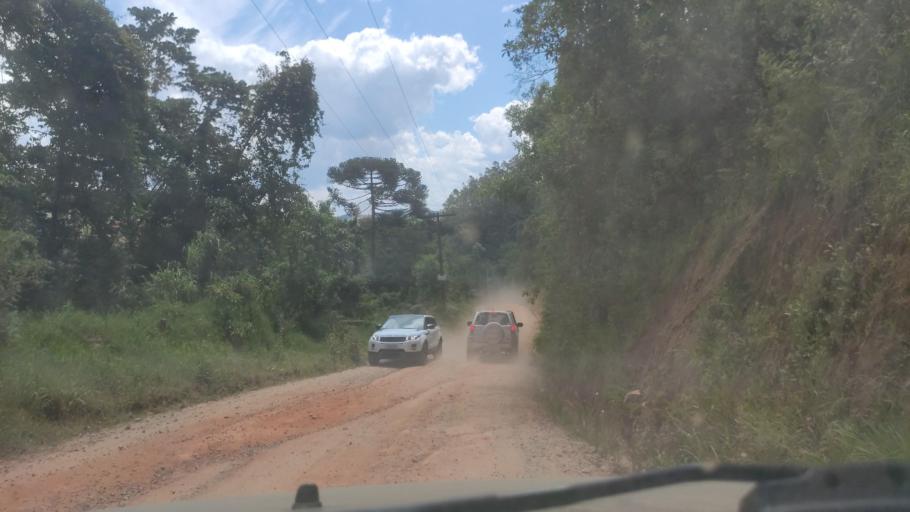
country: BR
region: Minas Gerais
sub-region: Cambui
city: Cambui
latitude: -22.7038
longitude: -46.0155
